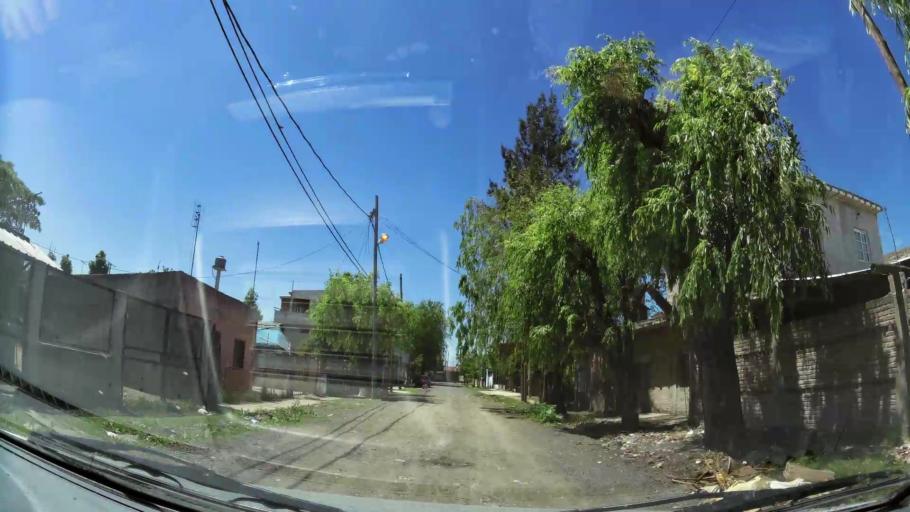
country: AR
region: Buenos Aires
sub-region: Partido de Quilmes
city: Quilmes
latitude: -34.7231
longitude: -58.3241
